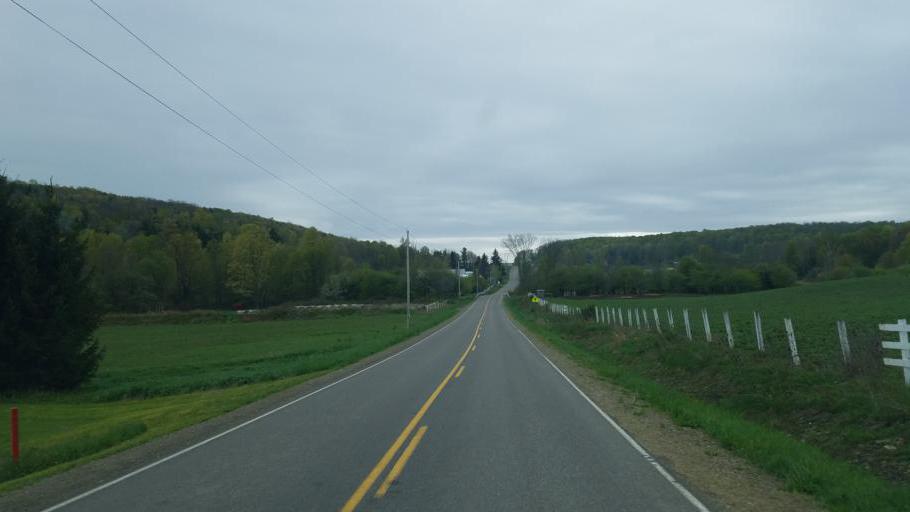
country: US
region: Pennsylvania
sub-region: Tioga County
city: Westfield
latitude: 42.0490
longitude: -77.4665
